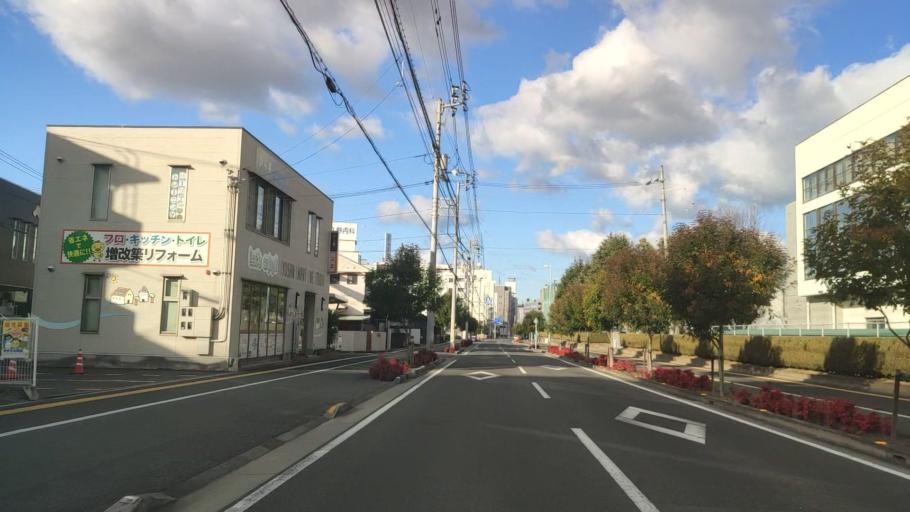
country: JP
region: Ehime
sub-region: Shikoku-chuo Shi
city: Matsuyama
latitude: 33.8413
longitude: 132.7810
